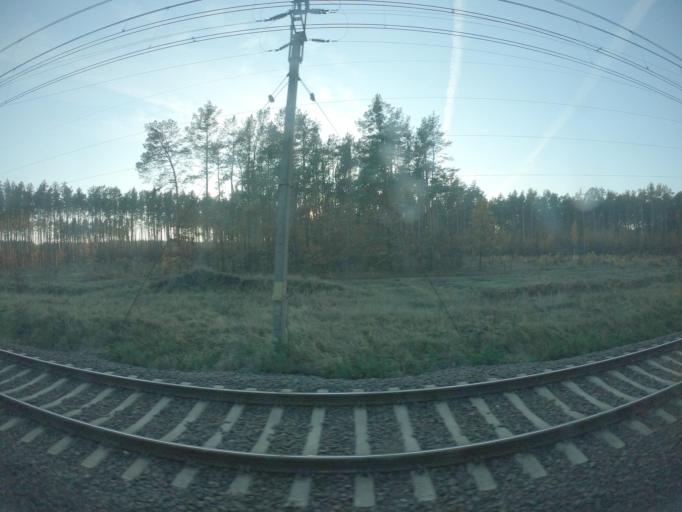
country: PL
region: Lubusz
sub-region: Powiat slubicki
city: Rzepin
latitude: 52.3096
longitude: 14.8638
